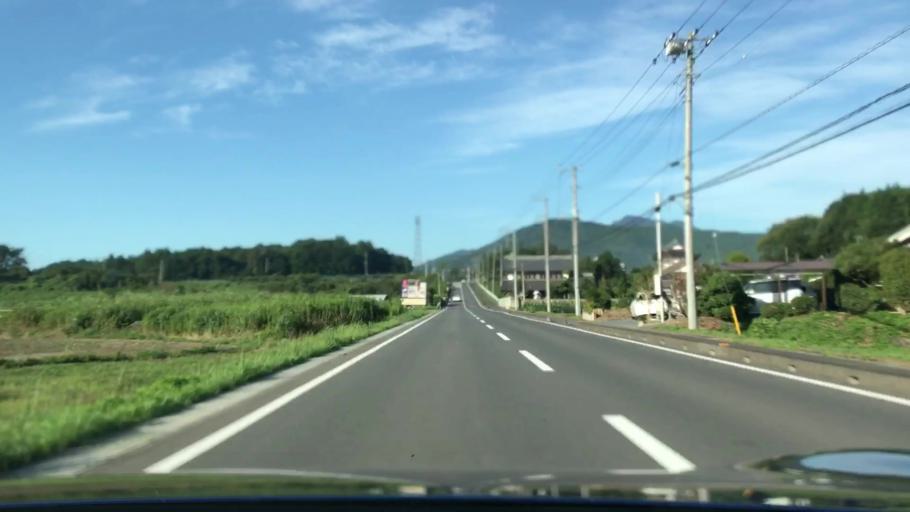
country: JP
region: Ibaraki
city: Makabe
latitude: 36.2664
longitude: 140.1787
